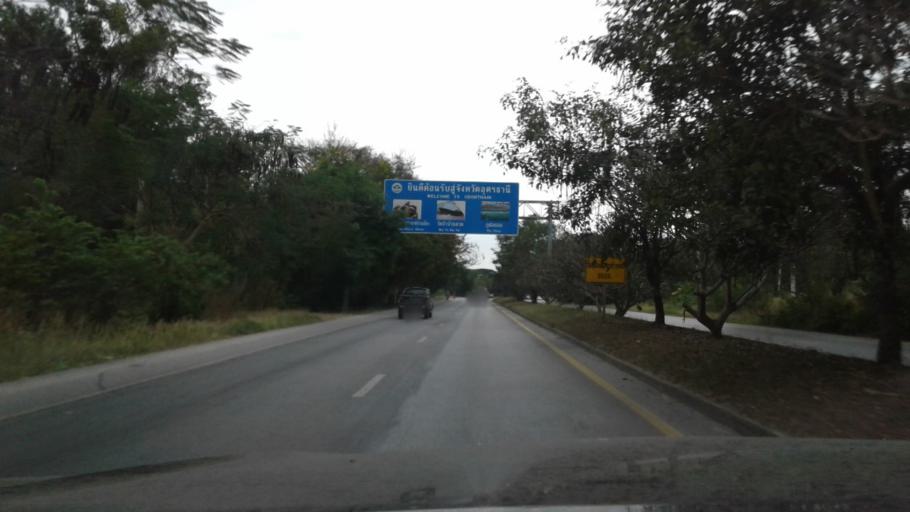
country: TH
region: Changwat Udon Thani
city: Udon Thani
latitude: 17.3597
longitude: 102.6938
